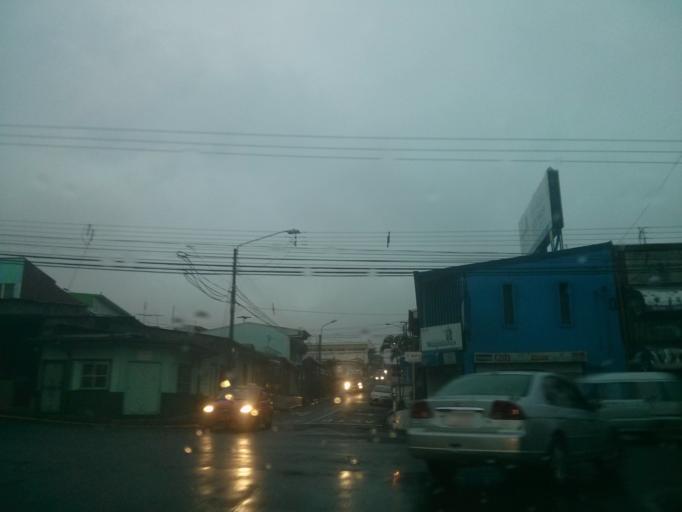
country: CR
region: Alajuela
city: Alajuela
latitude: 10.0131
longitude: -84.2181
